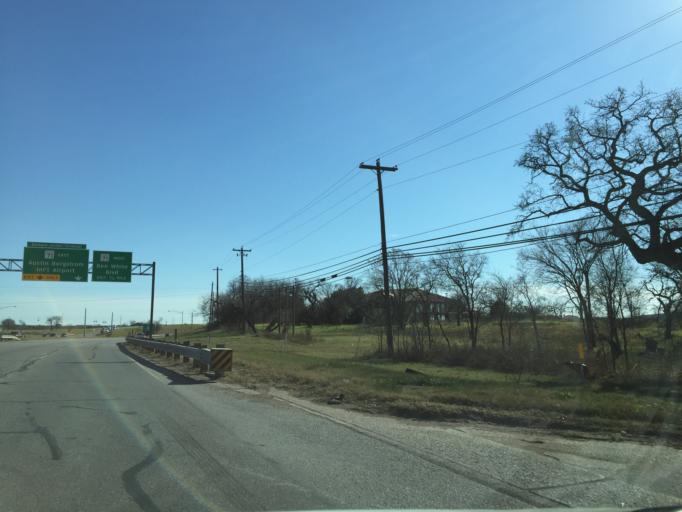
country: US
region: Texas
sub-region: Travis County
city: Austin
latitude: 30.2315
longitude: -97.6837
